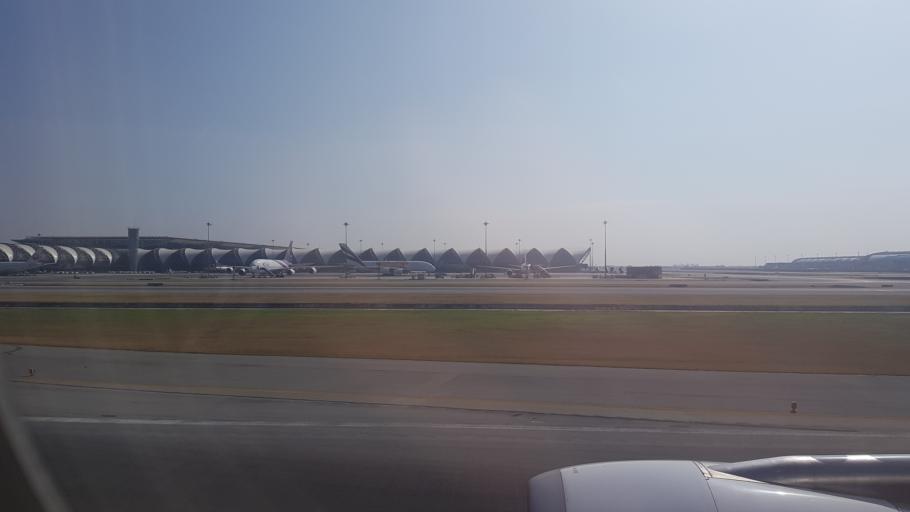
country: TH
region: Bangkok
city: Lat Krabang
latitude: 13.6895
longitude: 100.7395
